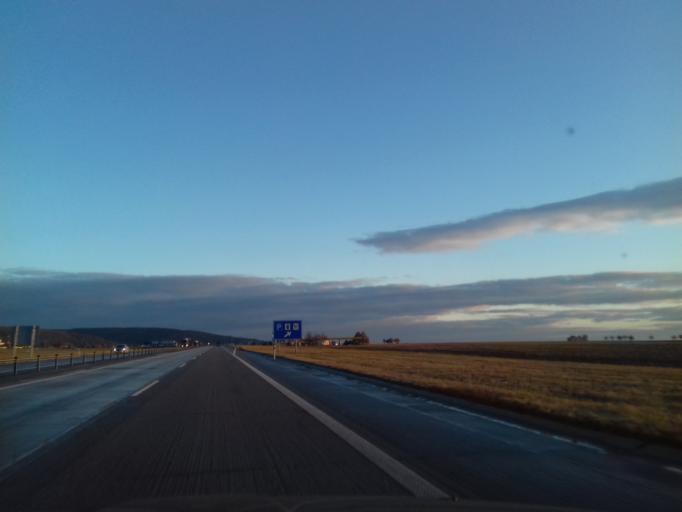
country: CZ
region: South Moravian
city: Pustimer
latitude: 49.3026
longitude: 17.0284
